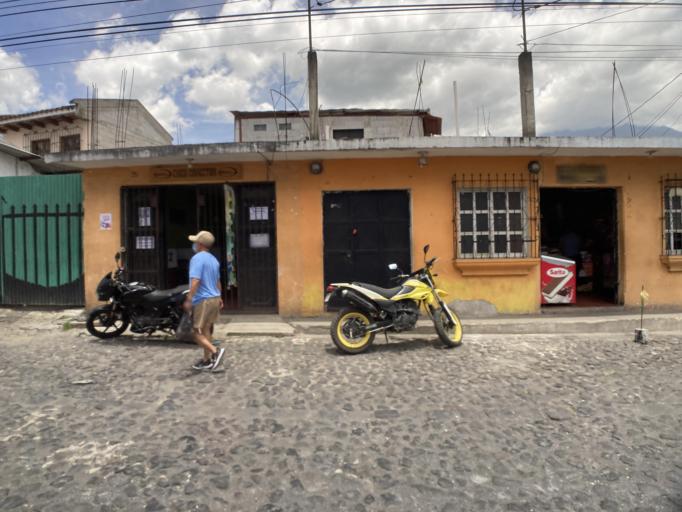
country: GT
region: Sacatepequez
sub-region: Municipio de Santa Maria de Jesus
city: Santa Maria de Jesus
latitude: 14.5323
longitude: -90.7370
